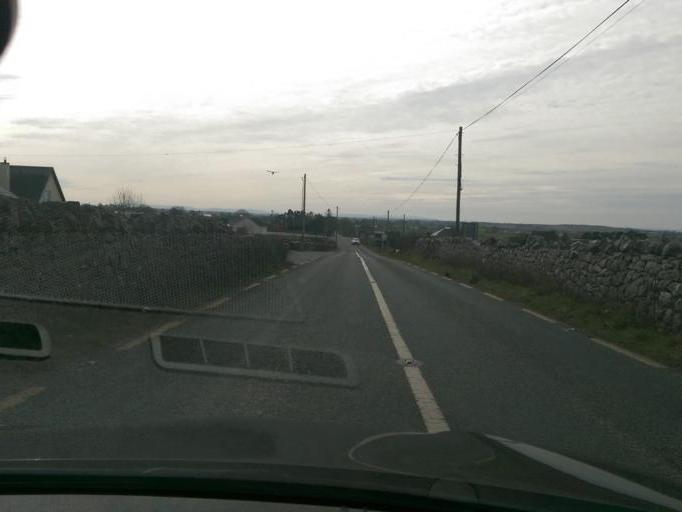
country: IE
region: Connaught
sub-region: County Galway
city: Tuam
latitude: 53.4033
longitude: -8.8275
